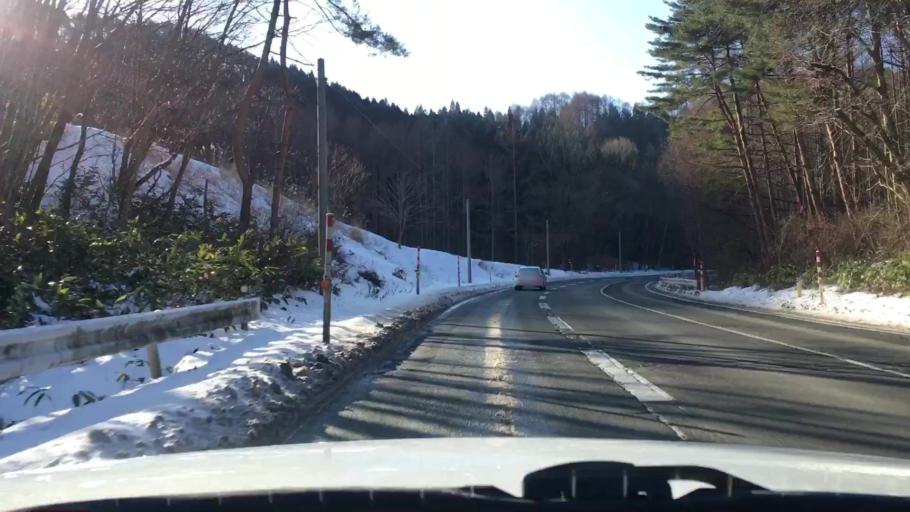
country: JP
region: Iwate
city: Morioka-shi
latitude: 39.6675
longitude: 141.3324
